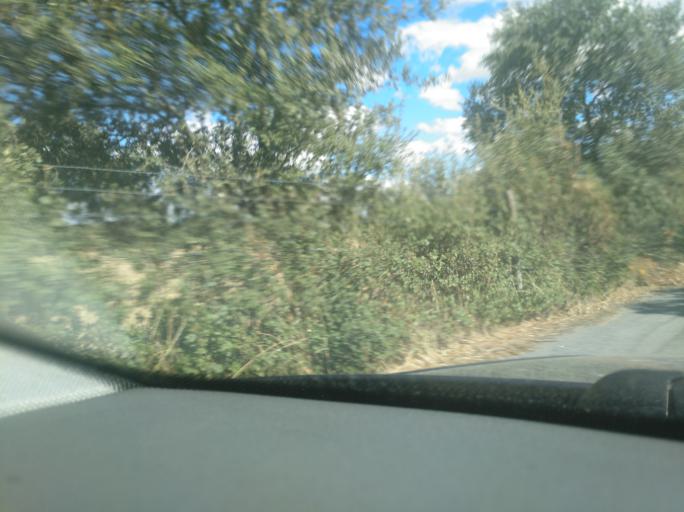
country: ES
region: Extremadura
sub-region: Provincia de Badajoz
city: La Codosera
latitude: 39.1174
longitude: -7.1520
